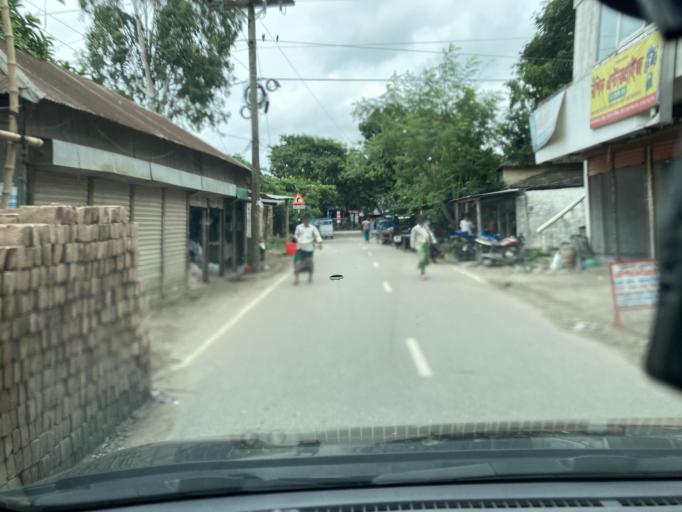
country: BD
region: Dhaka
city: Dohar
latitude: 23.7634
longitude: 90.1916
